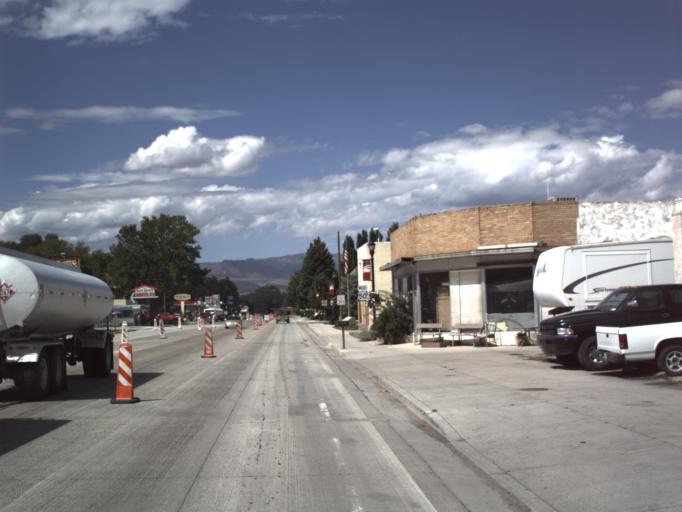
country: US
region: Utah
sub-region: Sevier County
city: Salina
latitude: 38.9576
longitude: -111.8575
